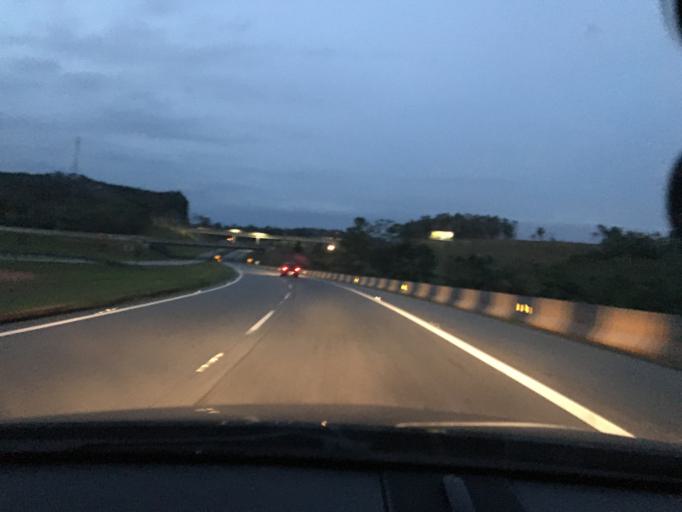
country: BR
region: Sao Paulo
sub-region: Santa Isabel
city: Santa Isabel
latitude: -23.3666
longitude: -46.1301
